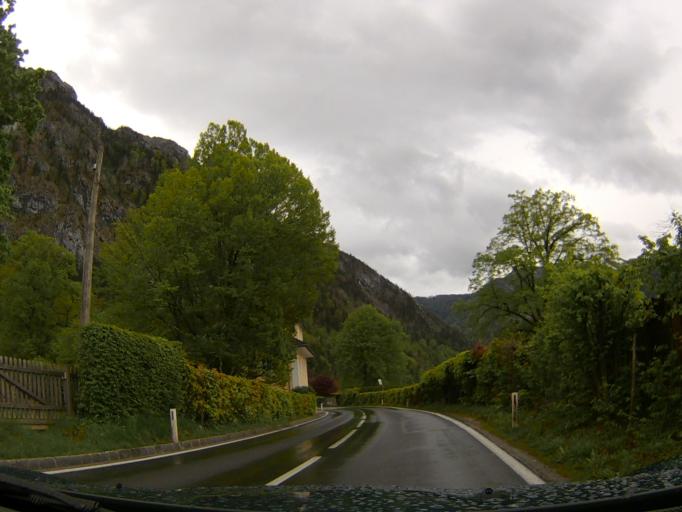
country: AT
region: Upper Austria
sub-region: Politischer Bezirk Vocklabruck
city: Steinbach am Attersee
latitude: 47.8091
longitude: 13.5478
